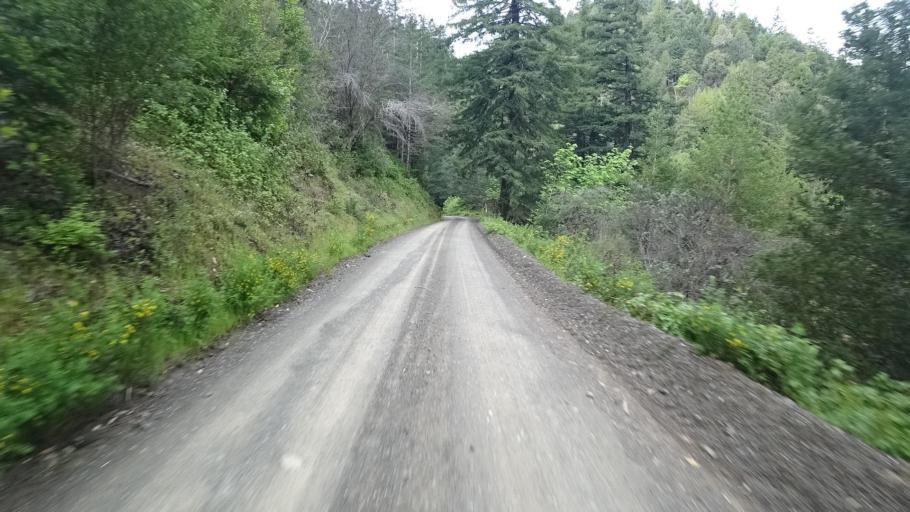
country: US
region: California
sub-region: Humboldt County
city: Redway
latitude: 40.3209
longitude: -123.8338
